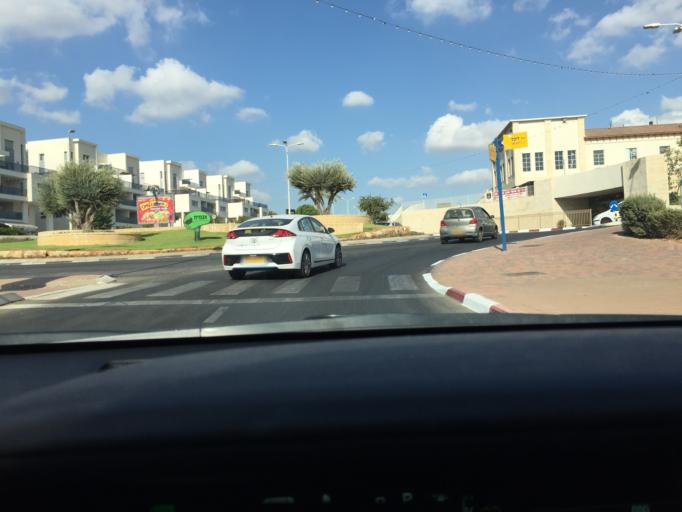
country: PS
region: West Bank
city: Budrus
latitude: 32.0065
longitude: 34.9504
